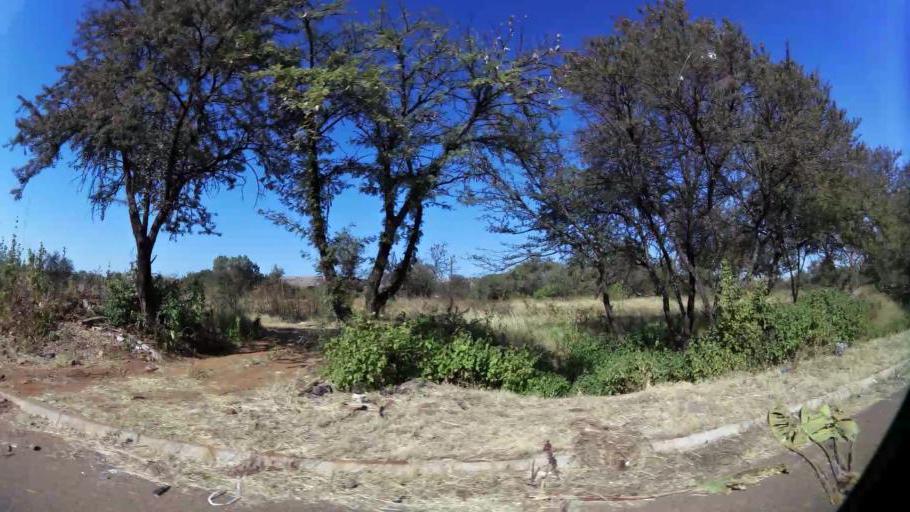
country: ZA
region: North-West
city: Ga-Rankuwa
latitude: -25.6611
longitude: 28.0886
